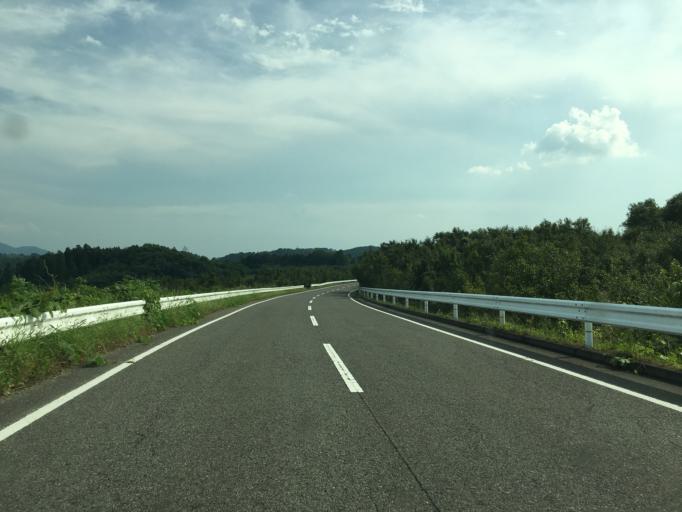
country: JP
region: Fukushima
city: Koriyama
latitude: 37.3825
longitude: 140.4444
